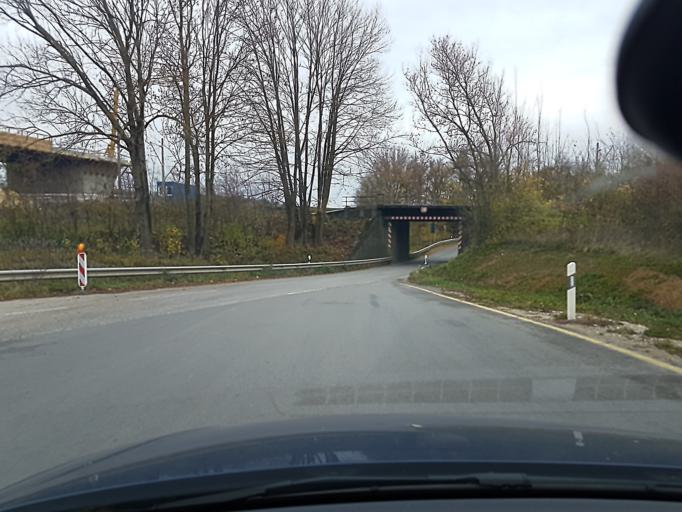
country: DE
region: Bavaria
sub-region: Upper Palatinate
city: Hagelstadt
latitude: 48.8859
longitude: 12.2128
